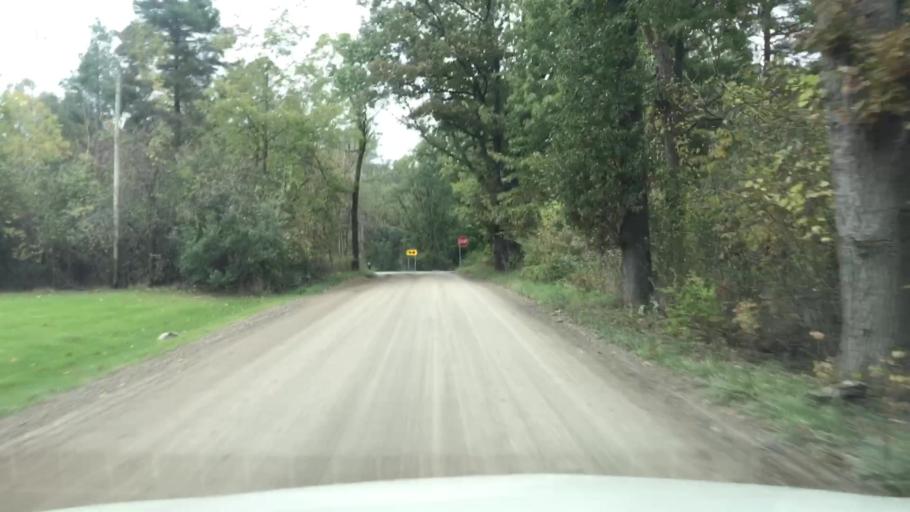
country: US
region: Michigan
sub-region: Oakland County
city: Rochester
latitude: 42.7395
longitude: -83.1262
